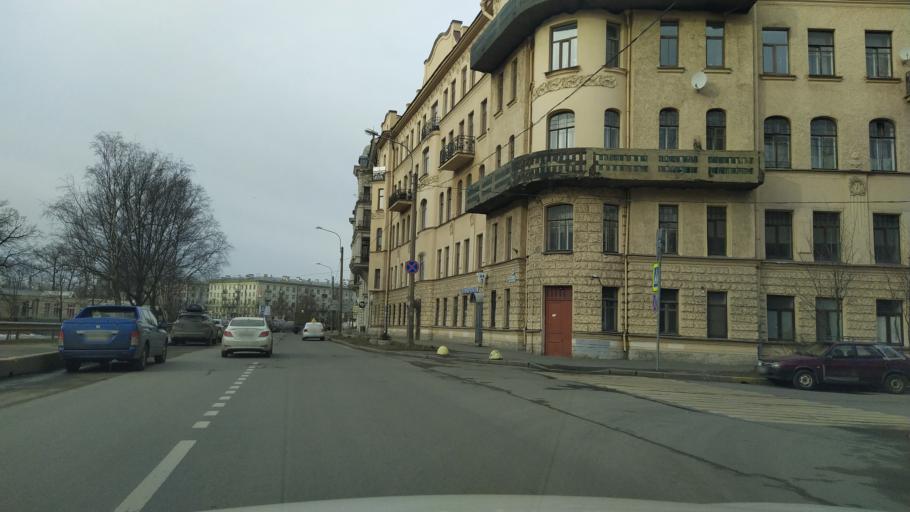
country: RU
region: Leningrad
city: Chernaya Rechka
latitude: 59.9854
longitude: 30.3058
